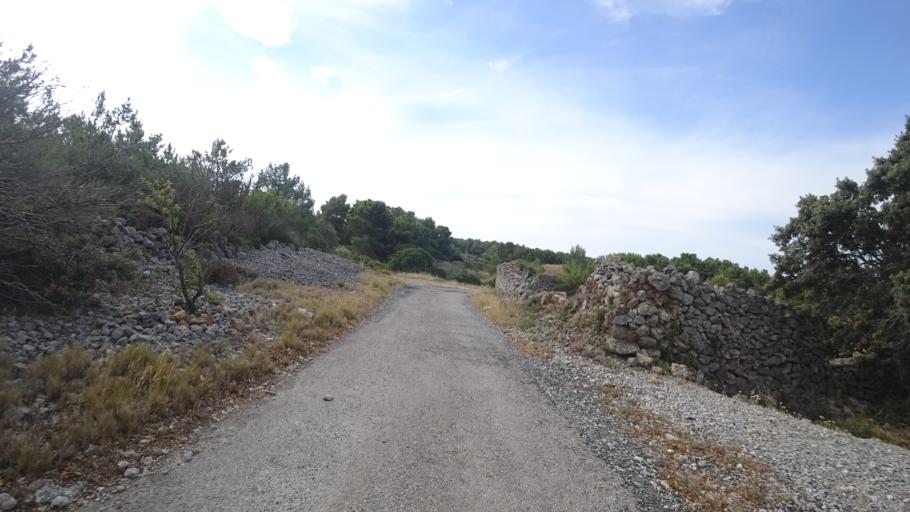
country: FR
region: Languedoc-Roussillon
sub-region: Departement de l'Aude
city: Leucate
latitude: 42.9039
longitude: 3.0234
